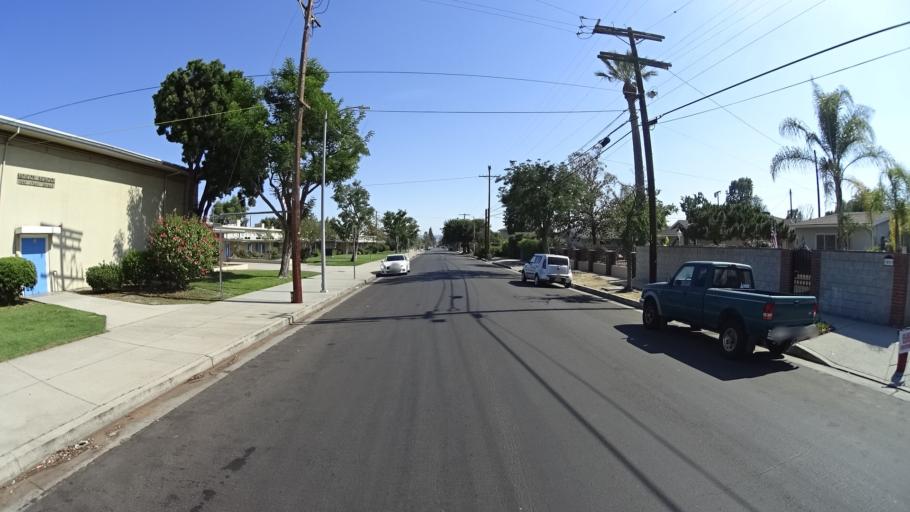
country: US
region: California
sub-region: Los Angeles County
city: Van Nuys
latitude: 34.2134
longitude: -118.4166
